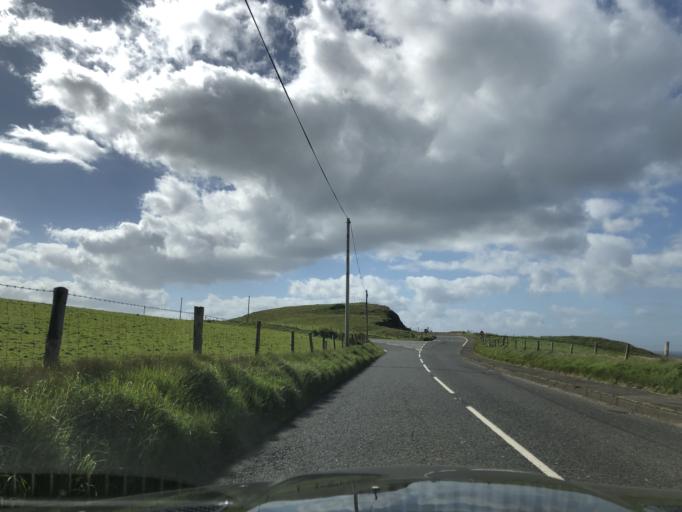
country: GB
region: Northern Ireland
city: Bushmills
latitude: 55.2124
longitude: -6.5711
